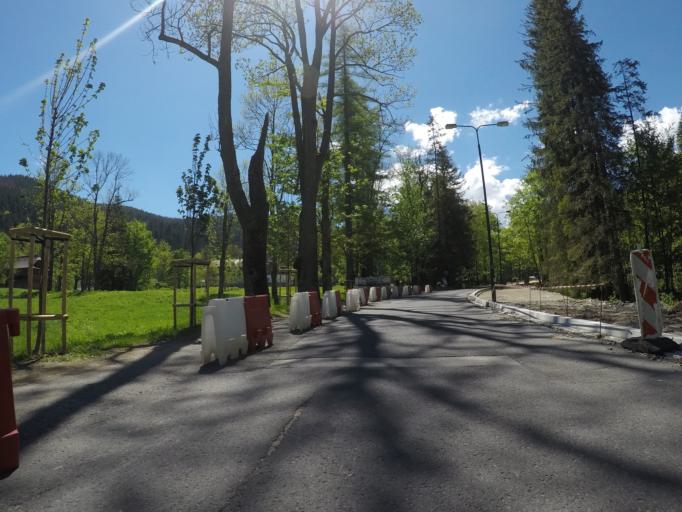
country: PL
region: Lesser Poland Voivodeship
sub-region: Powiat tatrzanski
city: Zakopane
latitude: 49.2731
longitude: 19.9810
